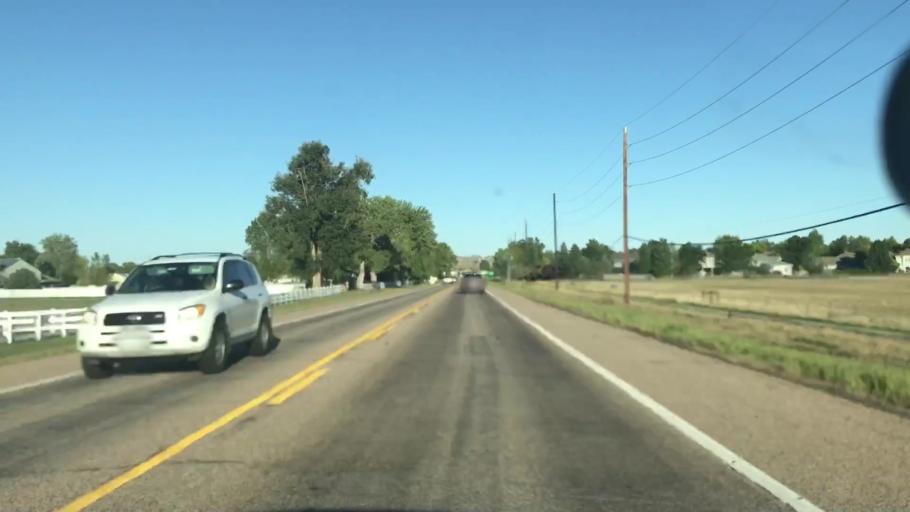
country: US
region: Colorado
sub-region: Boulder County
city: Lafayette
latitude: 39.9725
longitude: -105.1031
